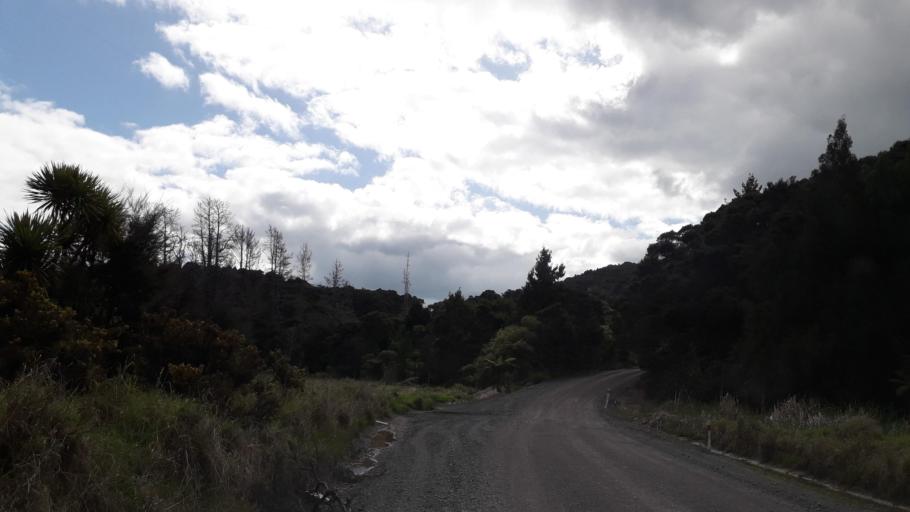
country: NZ
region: Northland
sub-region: Far North District
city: Paihia
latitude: -35.3080
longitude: 174.2208
